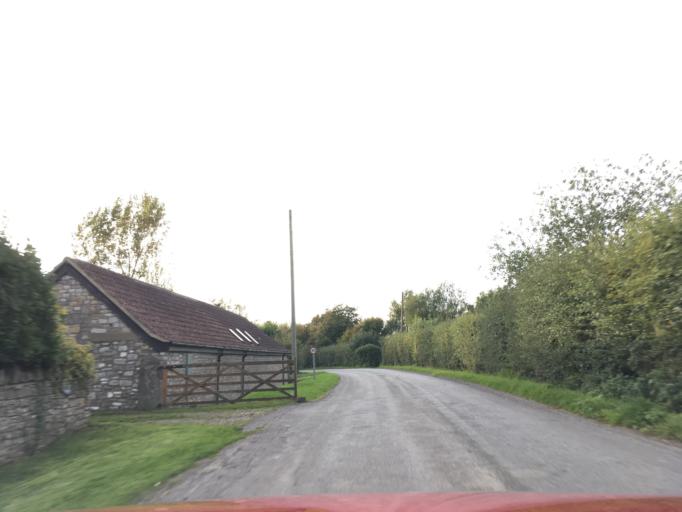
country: GB
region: England
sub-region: South Gloucestershire
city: Severn Beach
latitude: 51.5779
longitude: -2.6383
